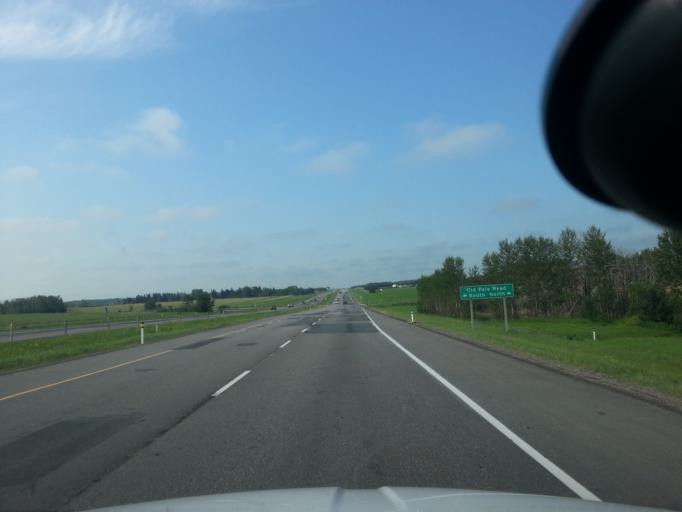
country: CA
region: Alberta
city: Penhold
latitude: 52.0871
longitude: -113.8547
